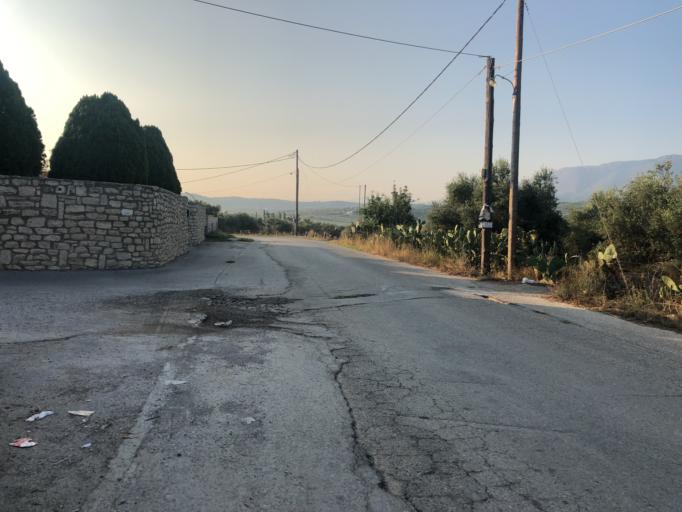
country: GR
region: Crete
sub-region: Nomos Chanias
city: Georgioupolis
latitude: 35.3482
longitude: 24.2855
